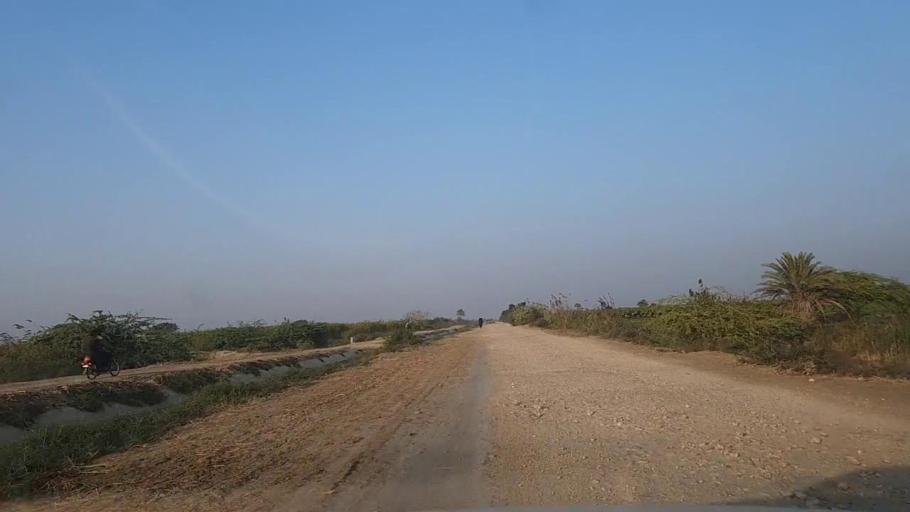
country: PK
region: Sindh
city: Keti Bandar
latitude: 24.2752
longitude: 67.6833
